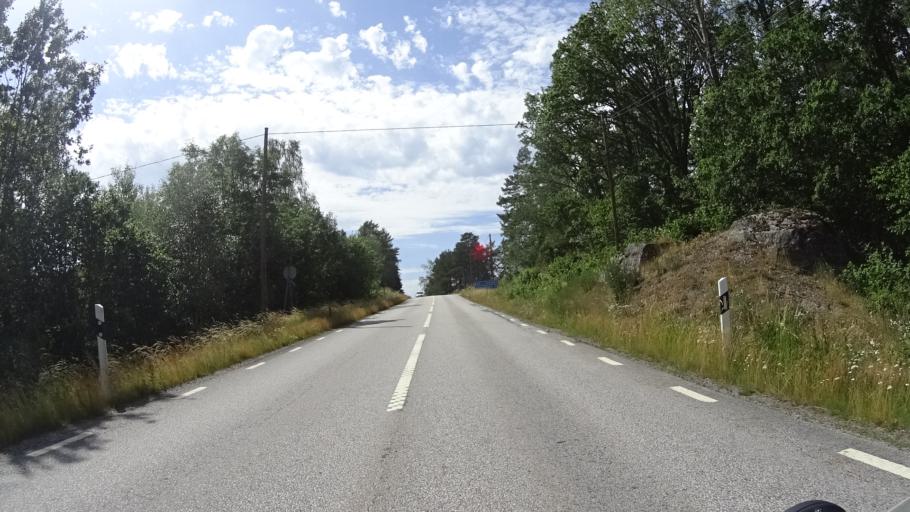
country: SE
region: Kalmar
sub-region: Vasterviks Kommun
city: Overum
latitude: 58.0788
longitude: 16.1632
